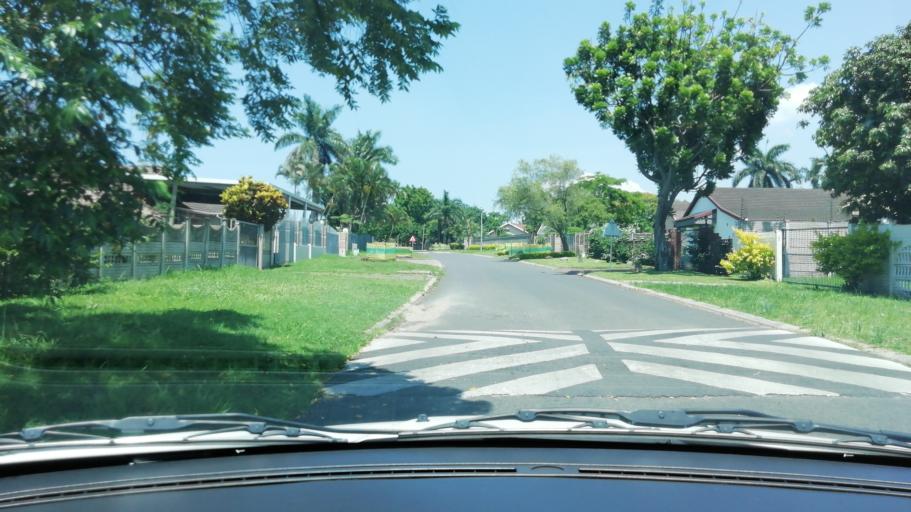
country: ZA
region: KwaZulu-Natal
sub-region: uThungulu District Municipality
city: Richards Bay
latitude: -28.7363
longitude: 32.0553
